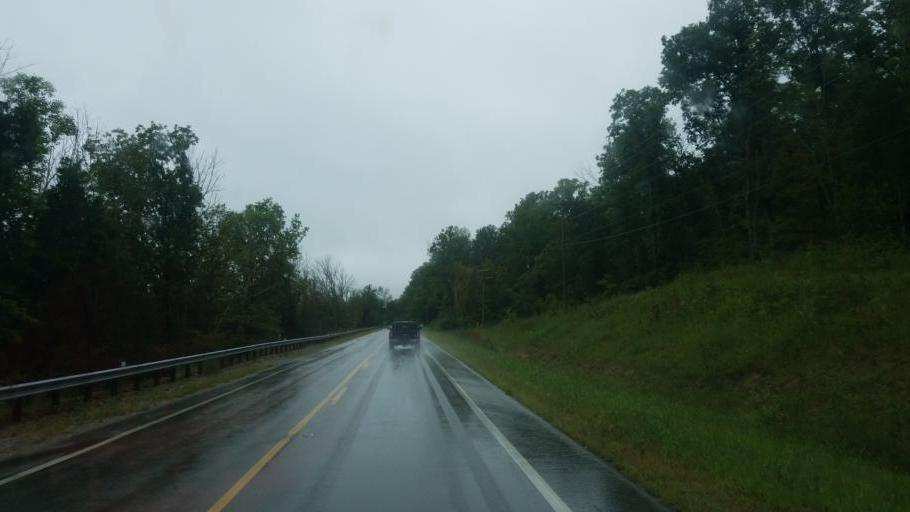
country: US
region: Ohio
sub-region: Adams County
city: West Union
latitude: 38.7943
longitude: -83.4659
